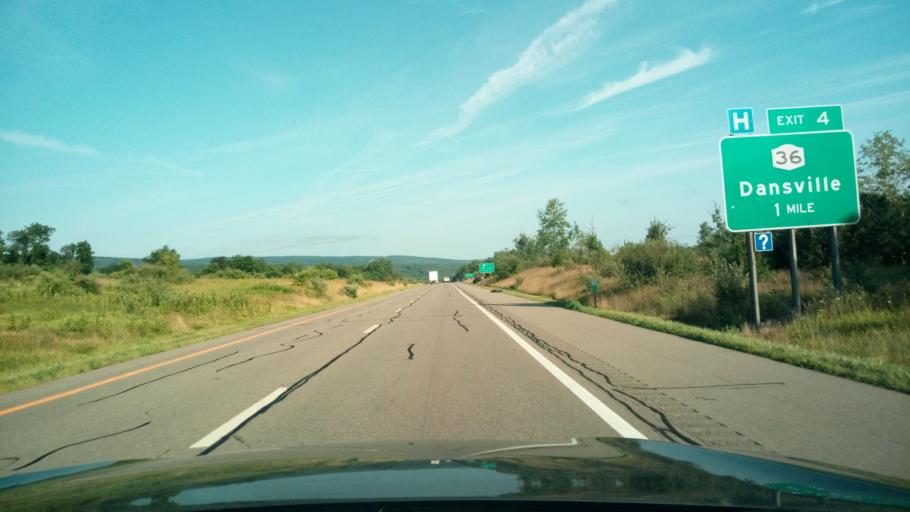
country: US
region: New York
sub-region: Livingston County
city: Dansville
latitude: 42.5388
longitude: -77.6845
